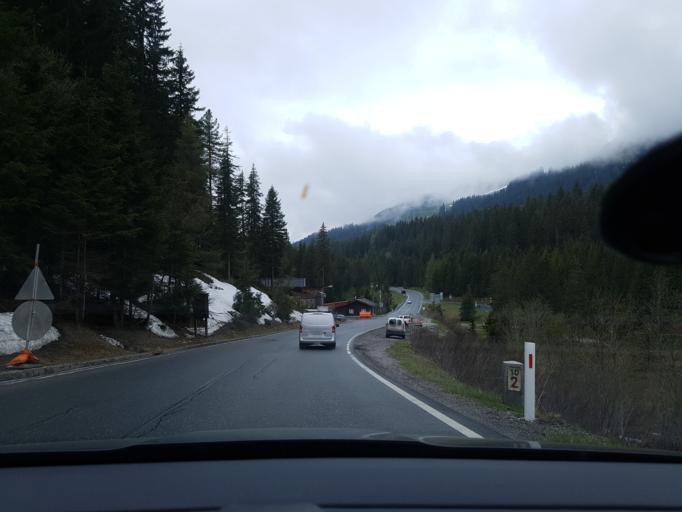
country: AT
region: Salzburg
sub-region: Politischer Bezirk Zell am See
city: Krimml
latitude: 47.2427
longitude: 12.1234
